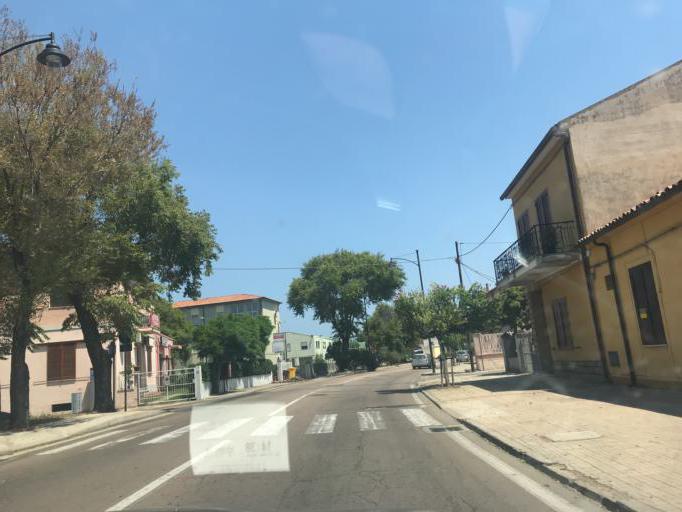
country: IT
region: Sardinia
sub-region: Provincia di Olbia-Tempio
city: Olbia
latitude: 40.9159
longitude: 9.4976
